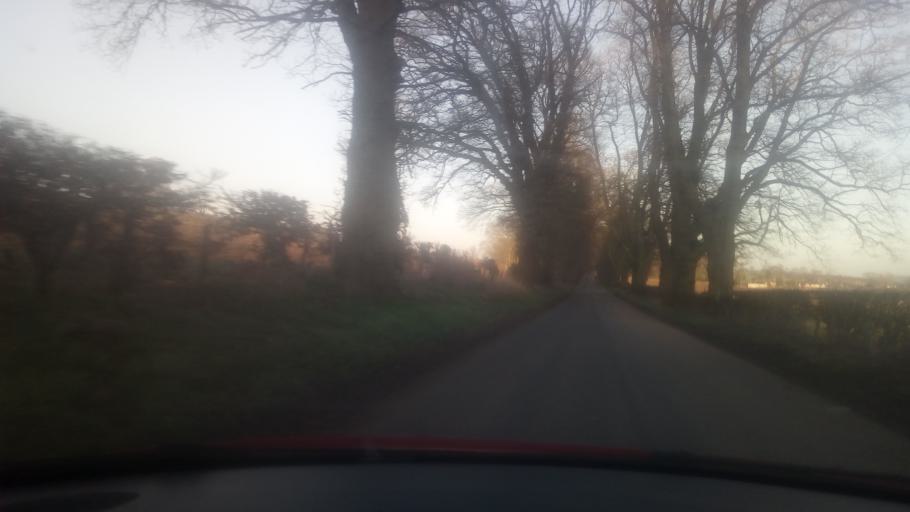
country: GB
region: Scotland
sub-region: The Scottish Borders
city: Jedburgh
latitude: 55.5219
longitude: -2.5289
